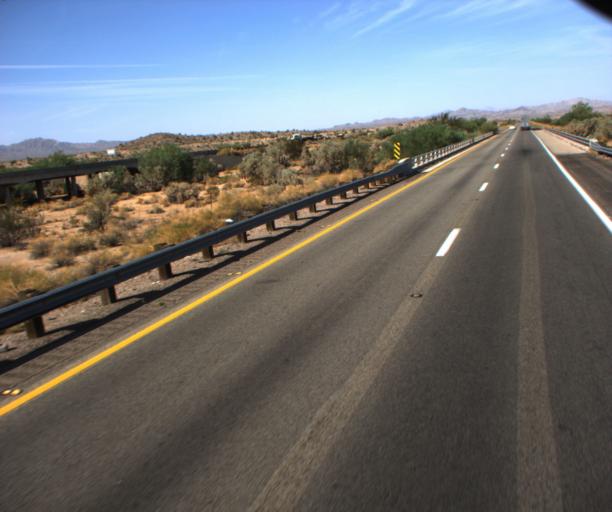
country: US
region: Arizona
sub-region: Mohave County
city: Desert Hills
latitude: 34.7477
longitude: -114.2301
